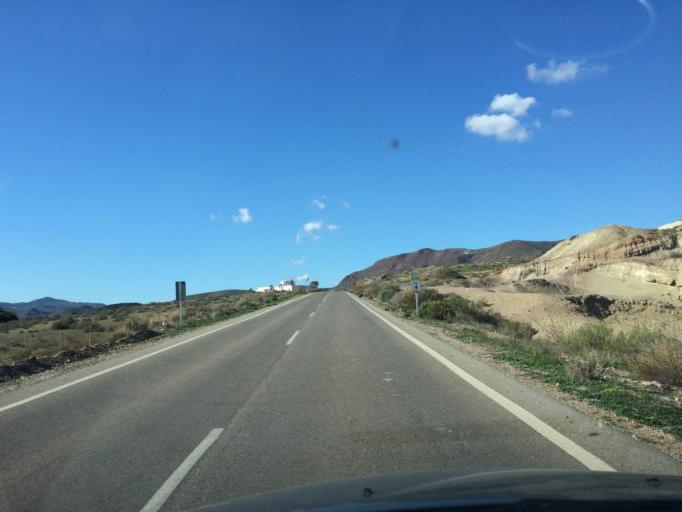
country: ES
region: Andalusia
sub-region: Provincia de Almeria
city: San Jose
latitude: 36.8061
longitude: -2.0736
